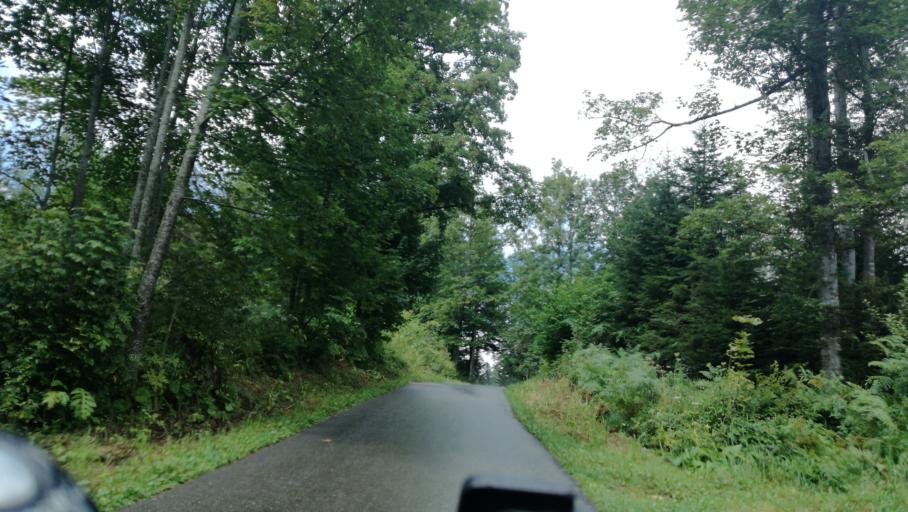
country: CH
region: Zug
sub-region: Zug
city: Walchwil
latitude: 47.1256
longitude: 8.5391
